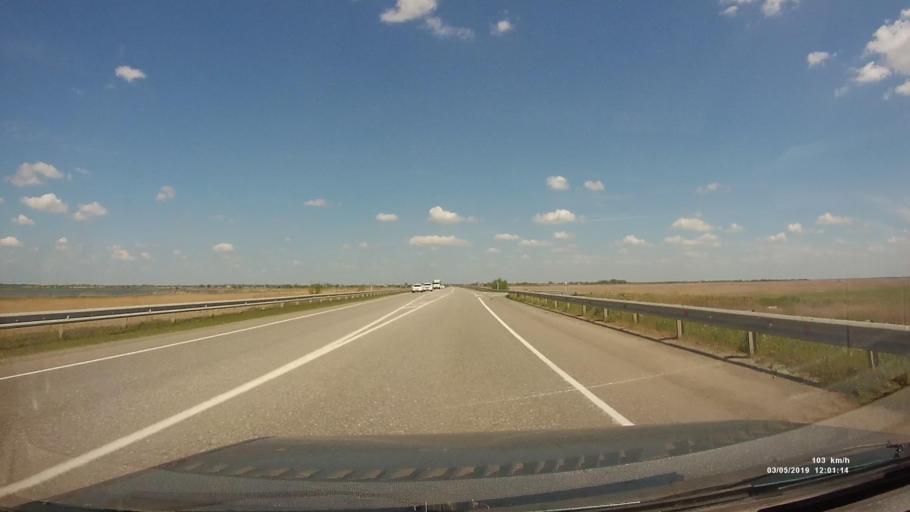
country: RU
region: Rostov
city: Bagayevskaya
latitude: 47.2601
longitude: 40.3488
